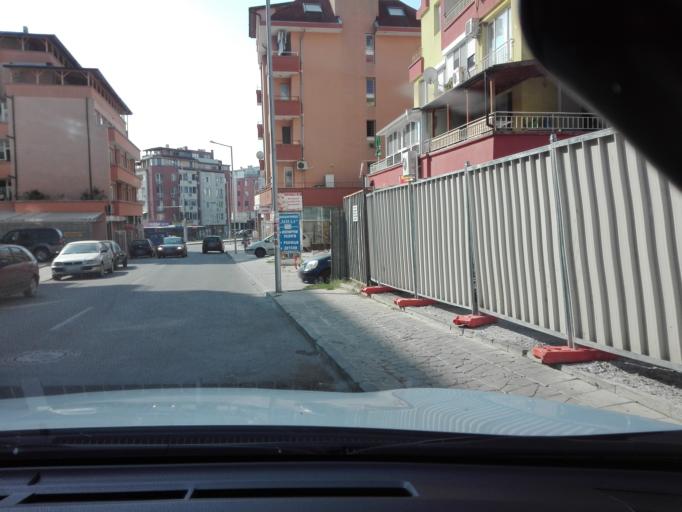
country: BG
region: Burgas
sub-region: Obshtina Burgas
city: Burgas
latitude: 42.4531
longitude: 27.4185
